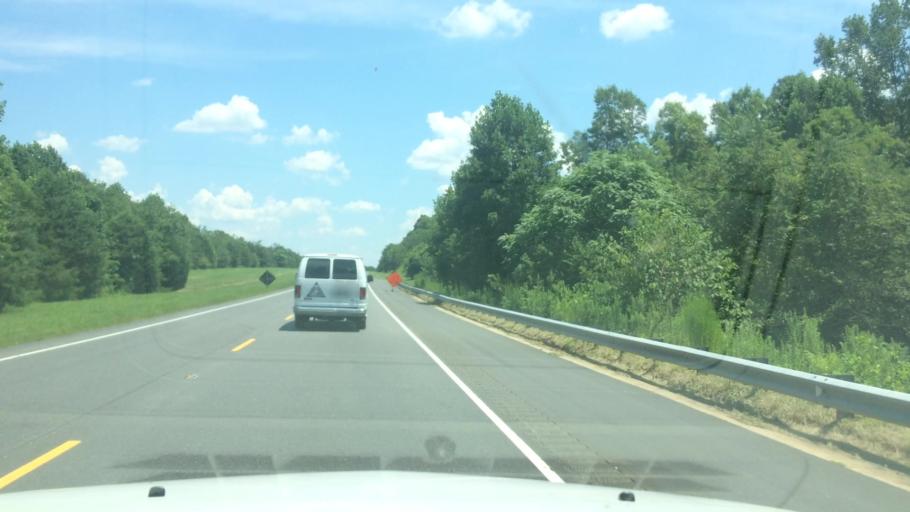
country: US
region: North Carolina
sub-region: Alexander County
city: Stony Point
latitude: 35.8155
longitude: -80.9932
